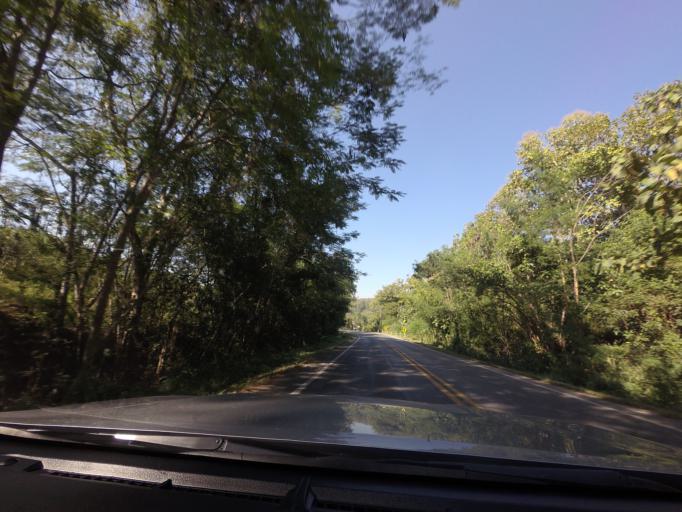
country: TH
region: Sukhothai
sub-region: Amphoe Si Satchanalai
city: Si Satchanalai
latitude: 17.6159
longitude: 99.7090
